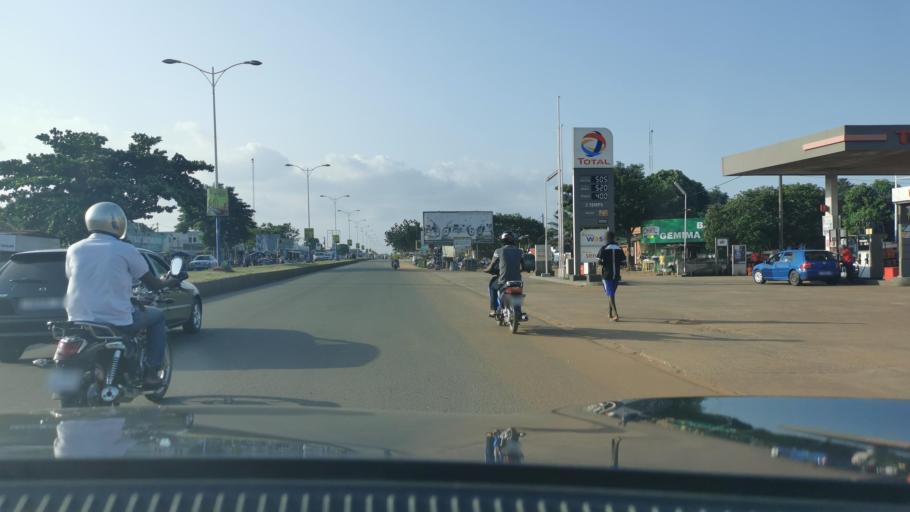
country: TG
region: Maritime
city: Lome
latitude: 6.2156
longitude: 1.2087
